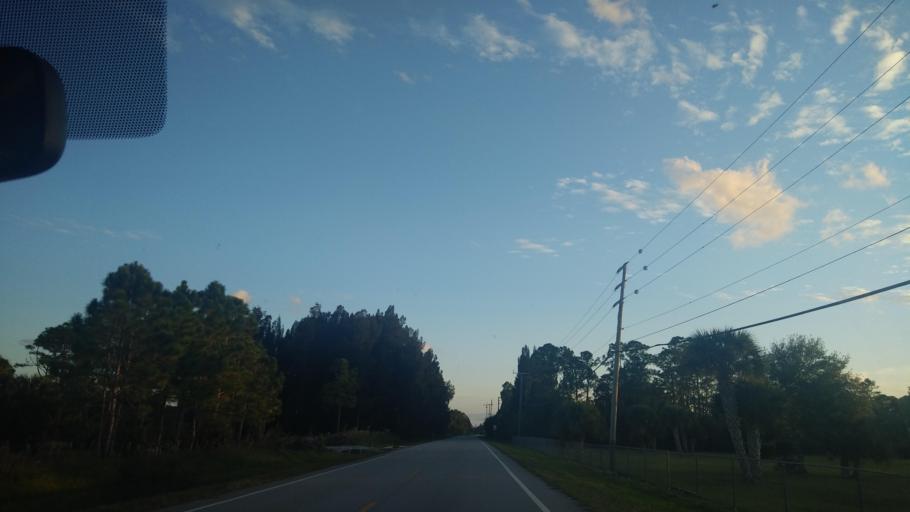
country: US
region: Florida
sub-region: Indian River County
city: Fellsmere
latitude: 27.7492
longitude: -80.5934
